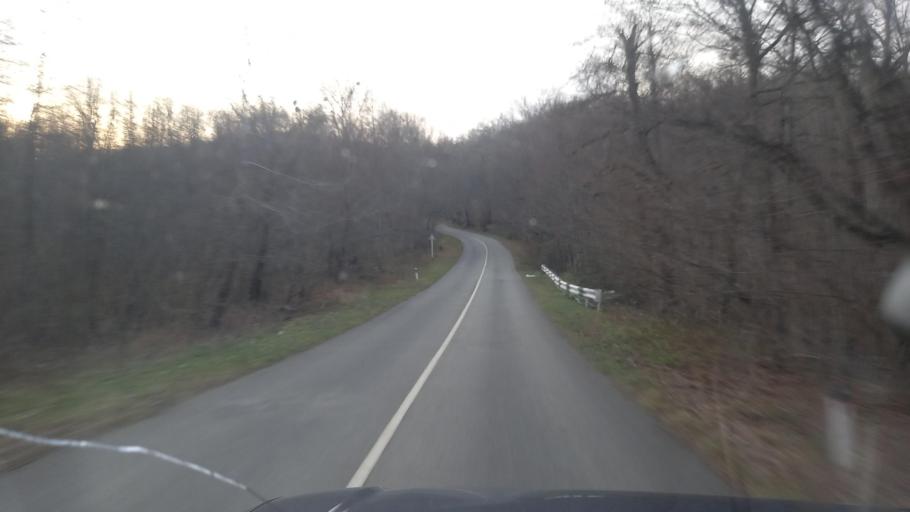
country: RU
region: Krasnodarskiy
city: Goryachiy Klyuch
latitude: 44.3869
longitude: 39.1876
